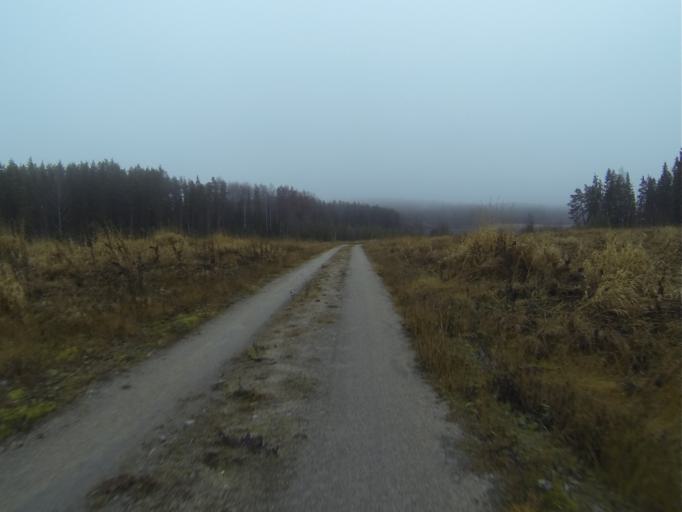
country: FI
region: Varsinais-Suomi
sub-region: Salo
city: Halikko
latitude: 60.4074
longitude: 22.9902
